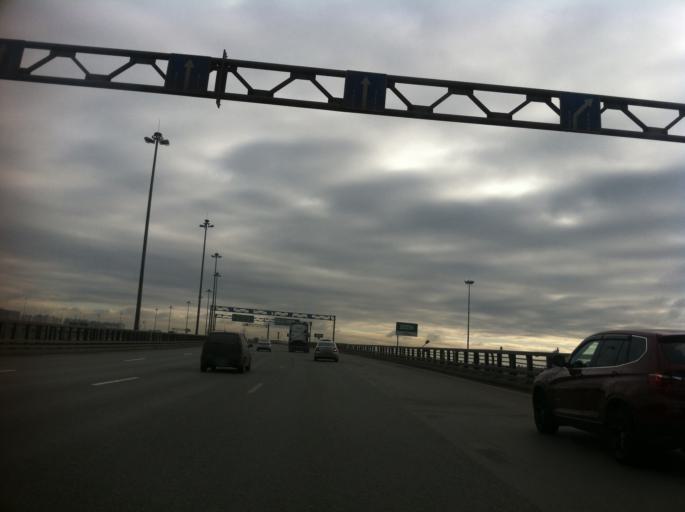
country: RU
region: St.-Petersburg
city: Kupchino
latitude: 59.8114
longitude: 30.3228
